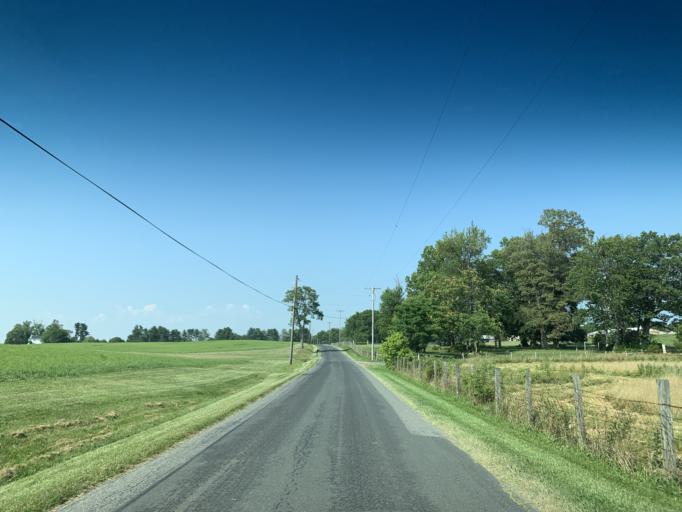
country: US
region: Virginia
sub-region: Loudoun County
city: University Center
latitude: 39.1068
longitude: -77.4676
